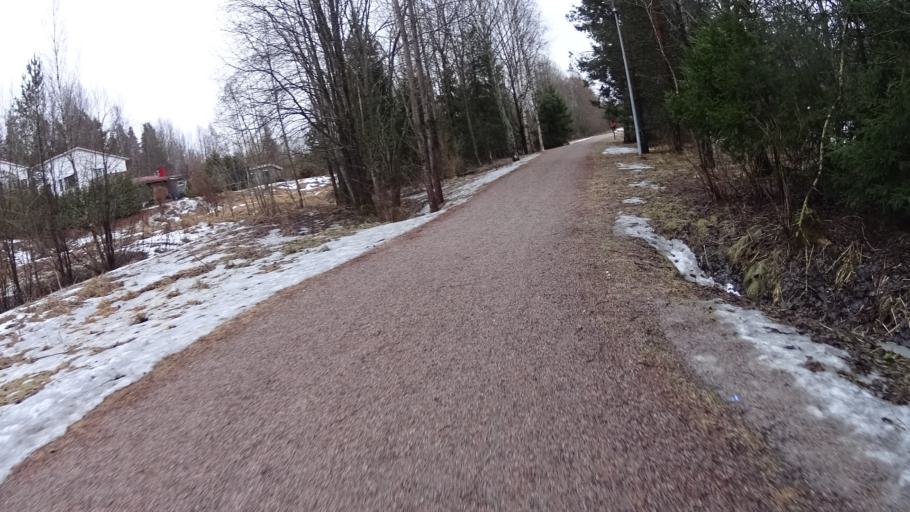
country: FI
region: Uusimaa
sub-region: Helsinki
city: Espoo
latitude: 60.2179
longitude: 24.6425
